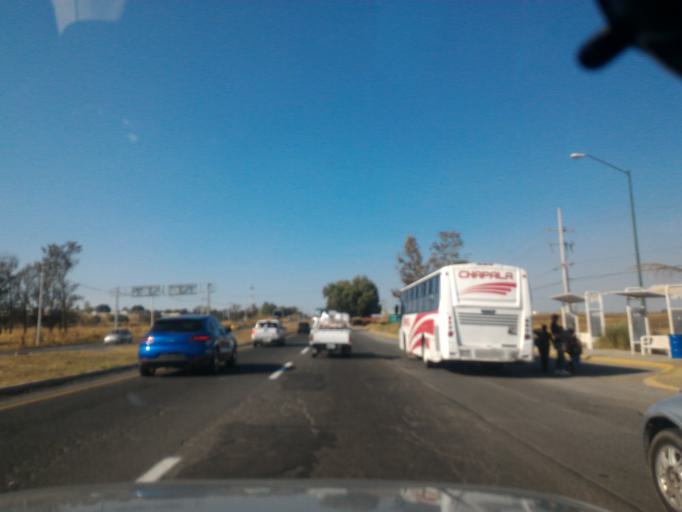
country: MX
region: Jalisco
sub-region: Ixtlahuacan de los Membrillos
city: Los Olivos
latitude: 20.4230
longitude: -103.2369
